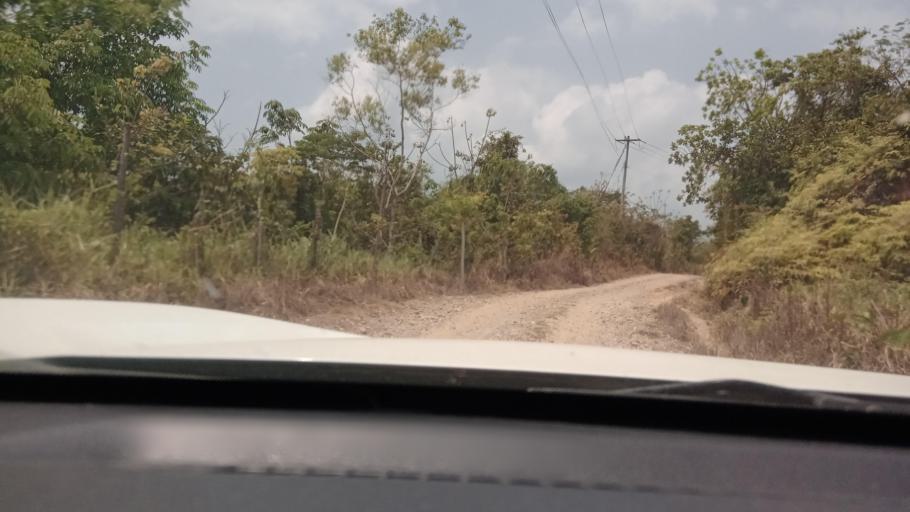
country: MX
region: Tabasco
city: Chontalpa
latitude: 17.5748
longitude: -93.7063
